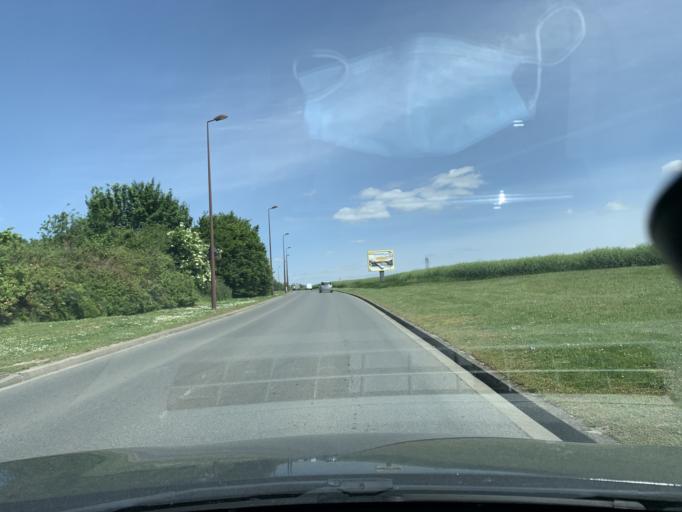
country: FR
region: Picardie
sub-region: Departement de l'Aisne
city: Saint-Quentin
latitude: 49.8650
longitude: 3.2821
